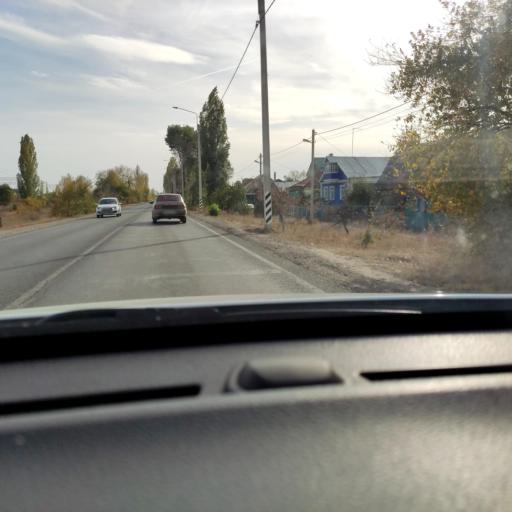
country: RU
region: Voronezj
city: Maslovka
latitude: 51.5734
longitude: 39.2466
